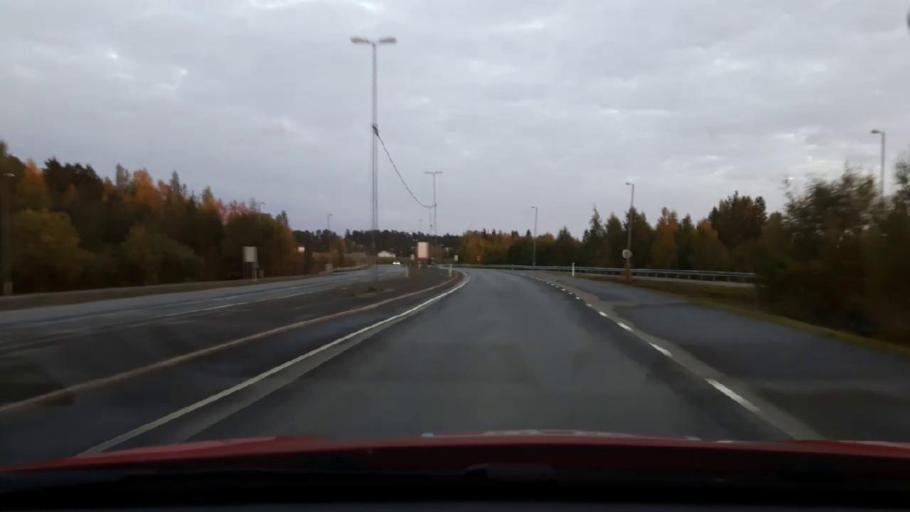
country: SE
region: Jaemtland
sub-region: OEstersunds Kommun
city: Ostersund
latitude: 63.2002
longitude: 14.6428
